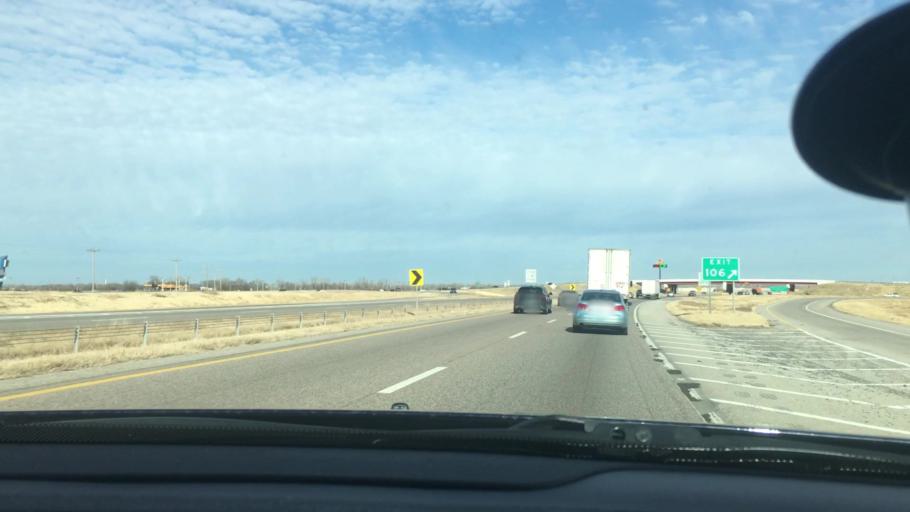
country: US
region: Oklahoma
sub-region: McClain County
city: Goldsby
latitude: 35.1765
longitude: -97.4943
